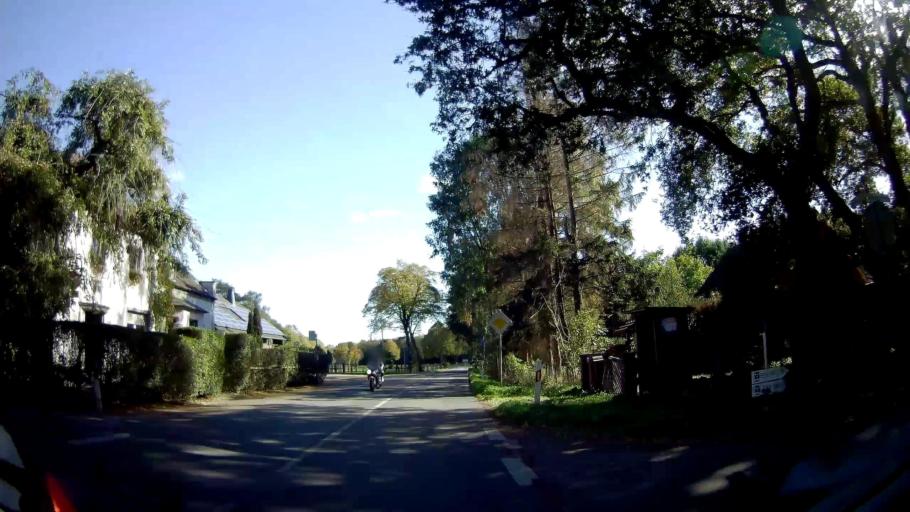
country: DE
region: North Rhine-Westphalia
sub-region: Regierungsbezirk Dusseldorf
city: Hunxe
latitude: 51.6150
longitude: 6.8080
